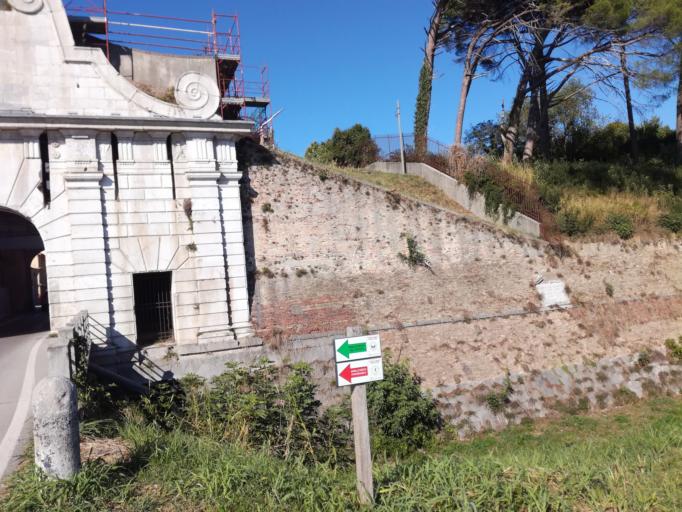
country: IT
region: Friuli Venezia Giulia
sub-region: Provincia di Udine
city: Palmanova
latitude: 45.9008
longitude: 13.3096
